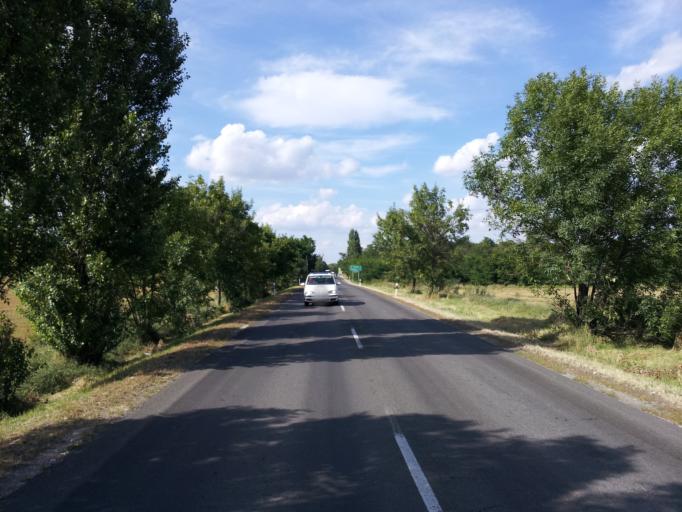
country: HU
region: Pest
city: Dunavarsany
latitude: 47.2569
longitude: 19.0260
